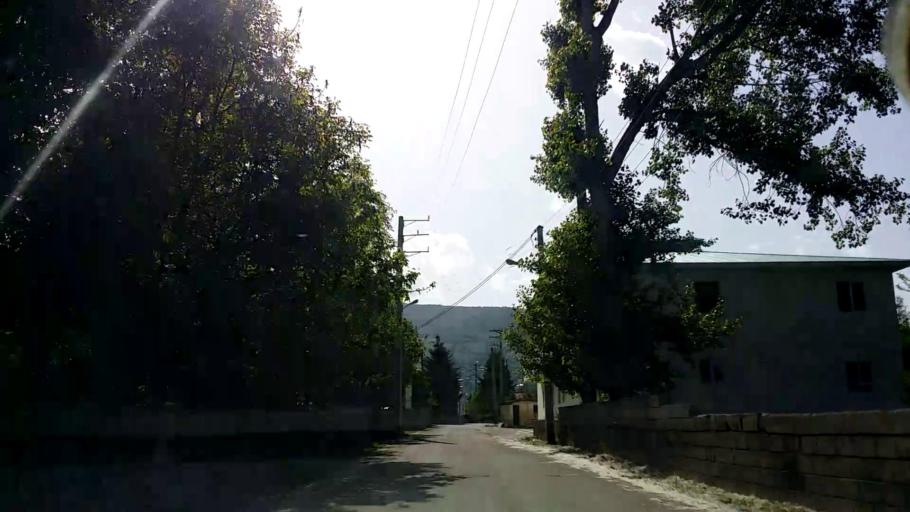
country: IR
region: Mazandaran
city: `Abbasabad
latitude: 36.5277
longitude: 51.1812
